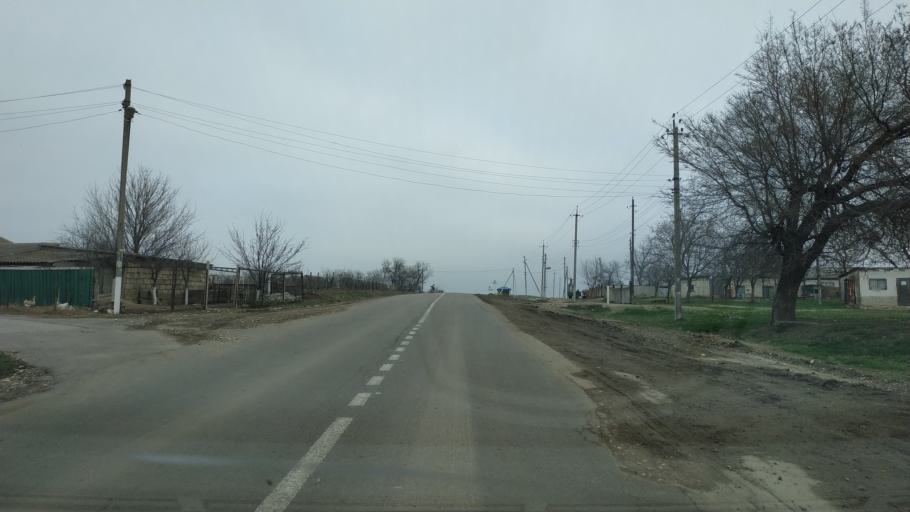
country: MD
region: Straseni
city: Taraclia
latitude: 45.9322
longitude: 28.5821
